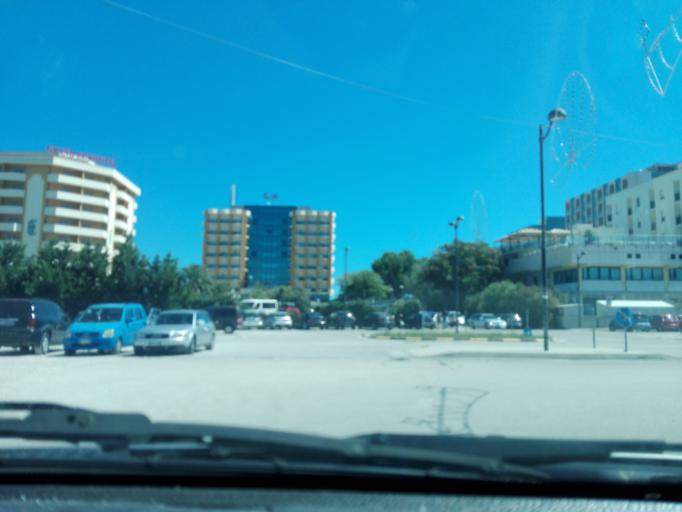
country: IT
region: Abruzzo
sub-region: Provincia di Pescara
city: Montesilvano Marina
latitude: 42.5235
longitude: 14.1521
